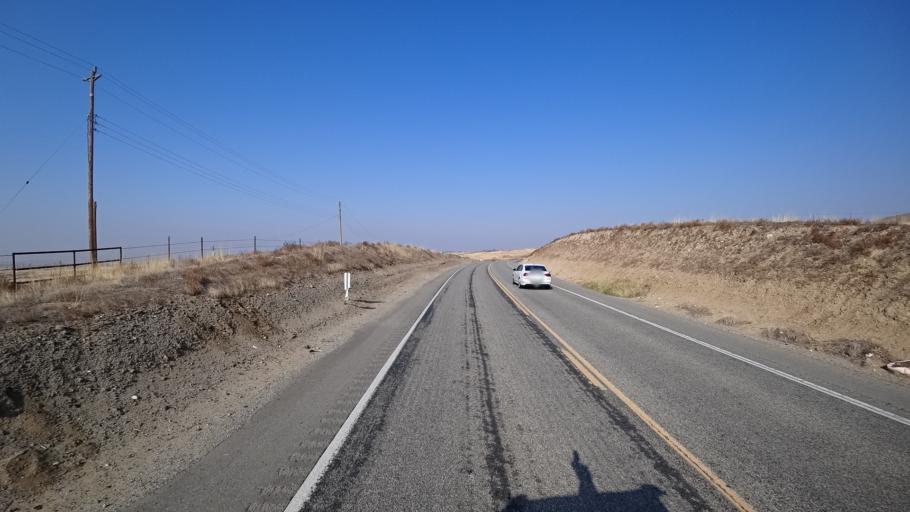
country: US
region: California
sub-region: Kern County
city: Lamont
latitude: 35.3788
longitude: -118.8494
